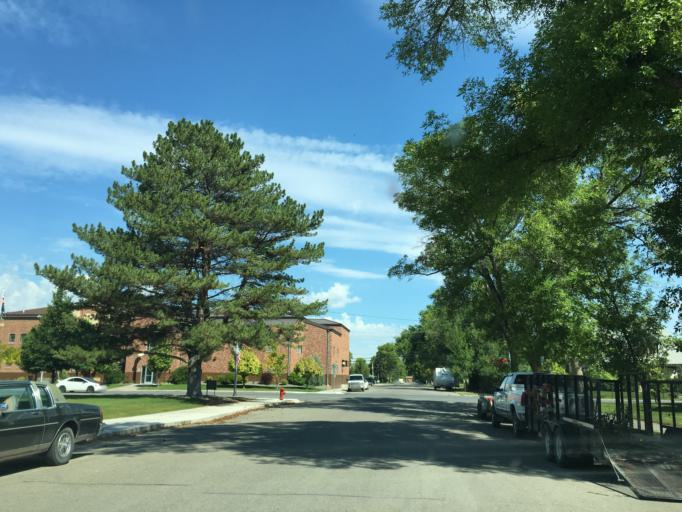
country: US
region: Montana
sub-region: Broadwater County
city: Townsend
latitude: 46.3209
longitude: -111.5145
